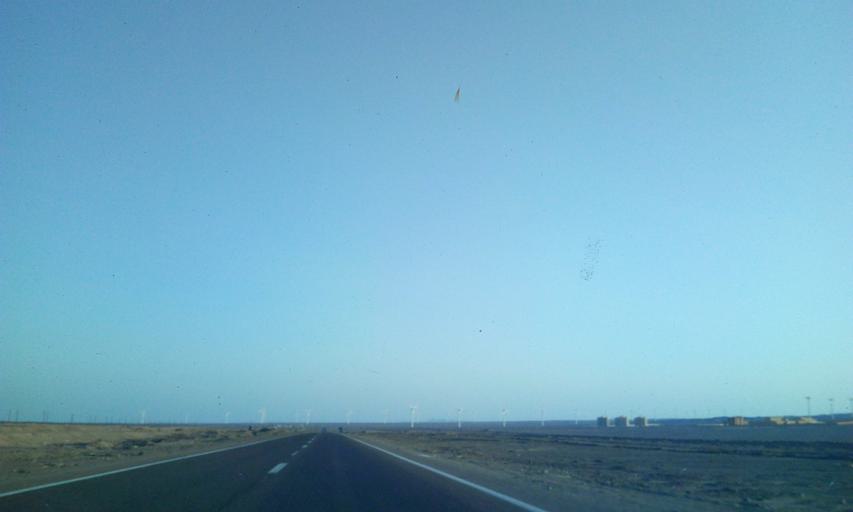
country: EG
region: South Sinai
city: Tor
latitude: 28.1003
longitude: 33.2535
